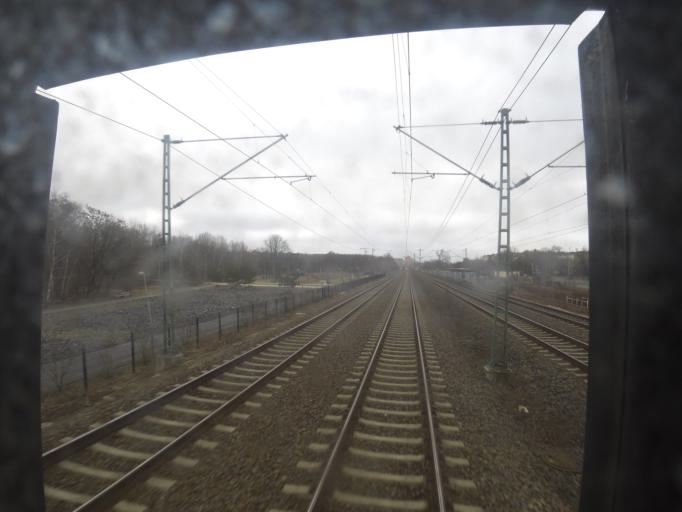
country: DE
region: Berlin
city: Tiergarten Bezirk
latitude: 52.4943
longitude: 13.3729
